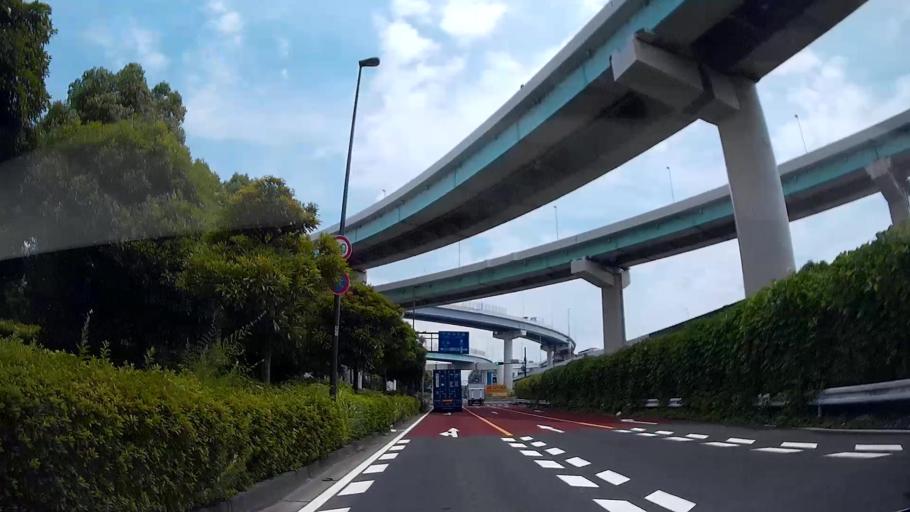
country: JP
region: Tokyo
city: Urayasu
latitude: 35.6442
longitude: 139.8112
